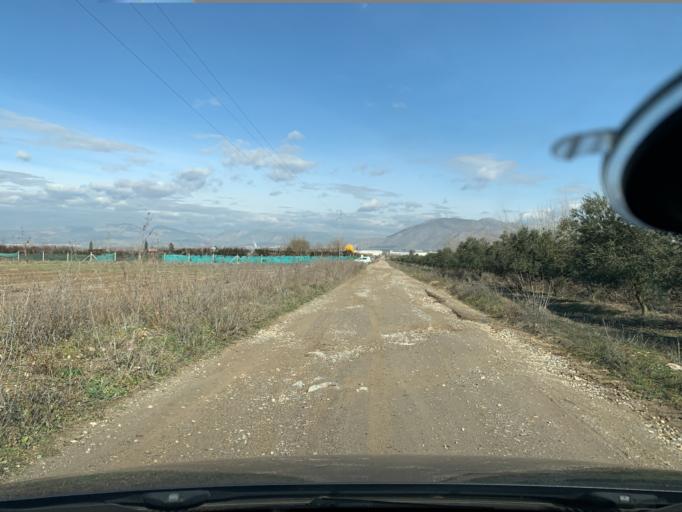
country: ES
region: Andalusia
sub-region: Provincia de Granada
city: Chauchina
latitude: 37.1786
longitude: -3.7512
